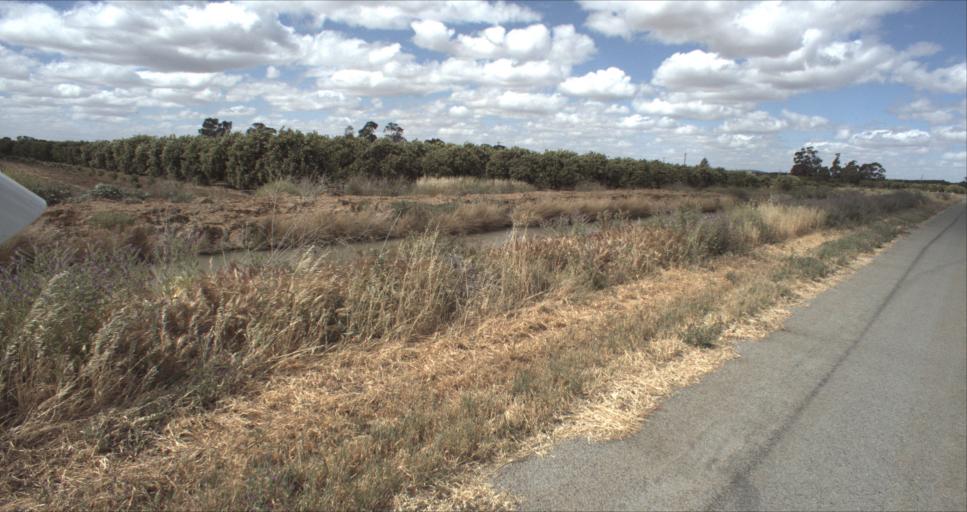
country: AU
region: New South Wales
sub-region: Leeton
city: Leeton
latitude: -34.5804
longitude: 146.3944
